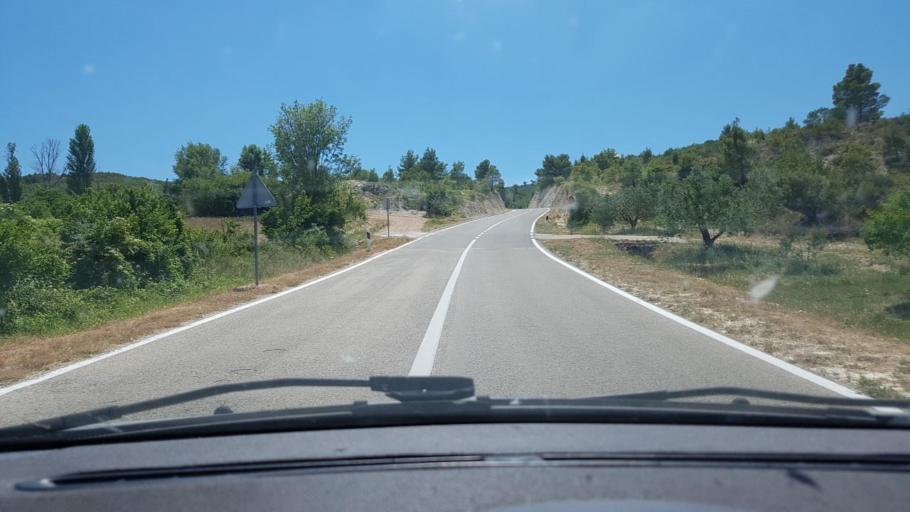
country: HR
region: Sibensko-Kniniska
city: Kistanje
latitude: 43.9067
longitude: 15.9143
